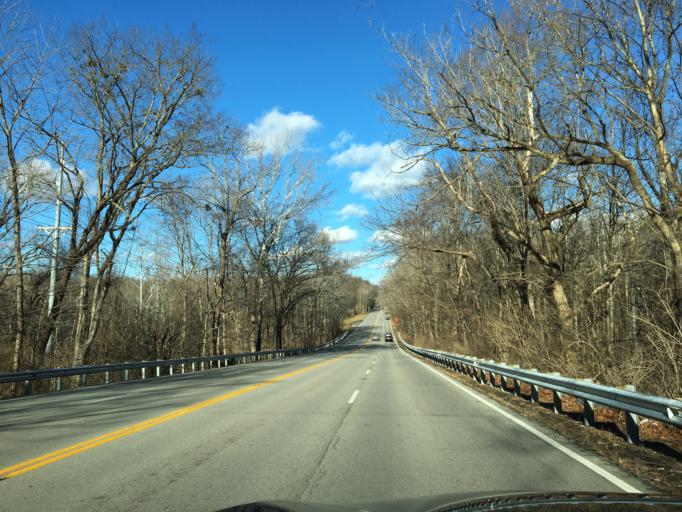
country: US
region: Kentucky
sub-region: Jefferson County
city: Barbourmeade
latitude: 38.3117
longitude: -85.6260
